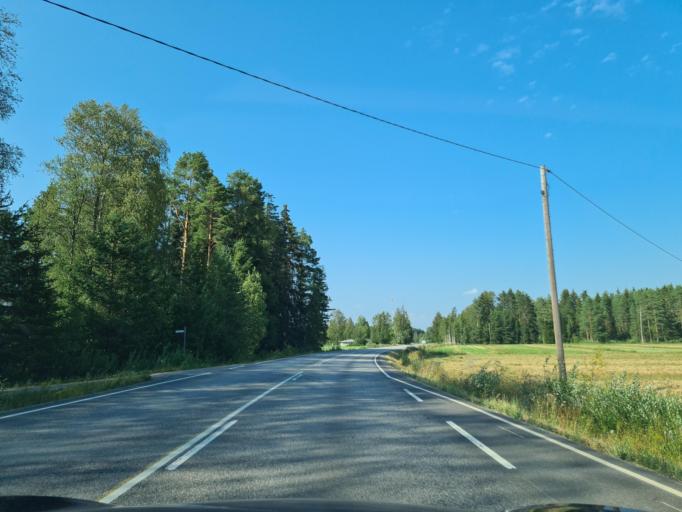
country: FI
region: Satakunta
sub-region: Pohjois-Satakunta
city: Kankaanpaeae
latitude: 61.9367
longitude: 22.5075
